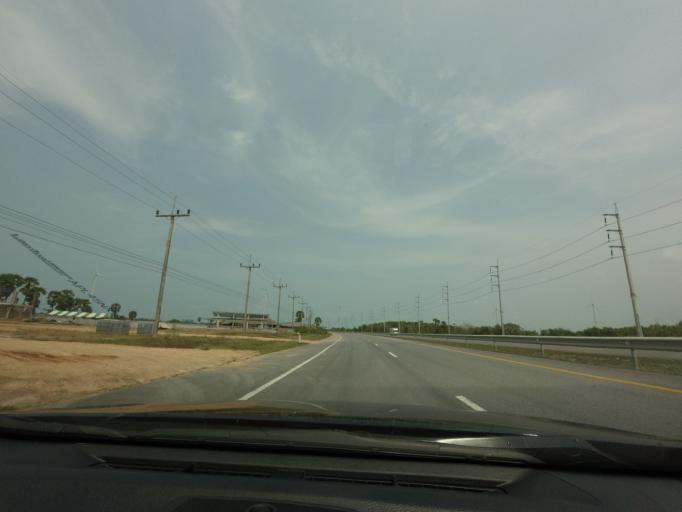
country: TH
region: Nakhon Si Thammarat
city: Hua Sai
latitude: 7.9984
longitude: 100.3083
